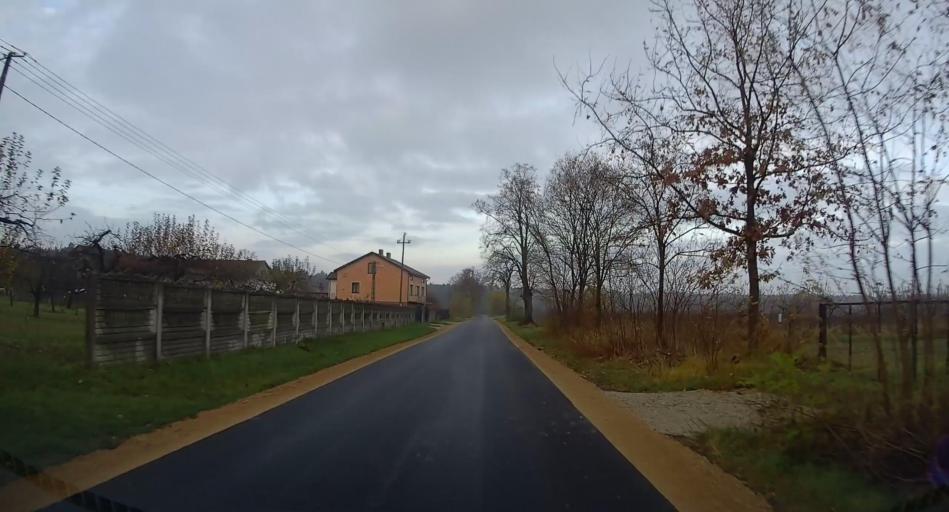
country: PL
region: Lodz Voivodeship
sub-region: Powiat skierniewicki
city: Kowiesy
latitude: 51.9275
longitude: 20.4029
